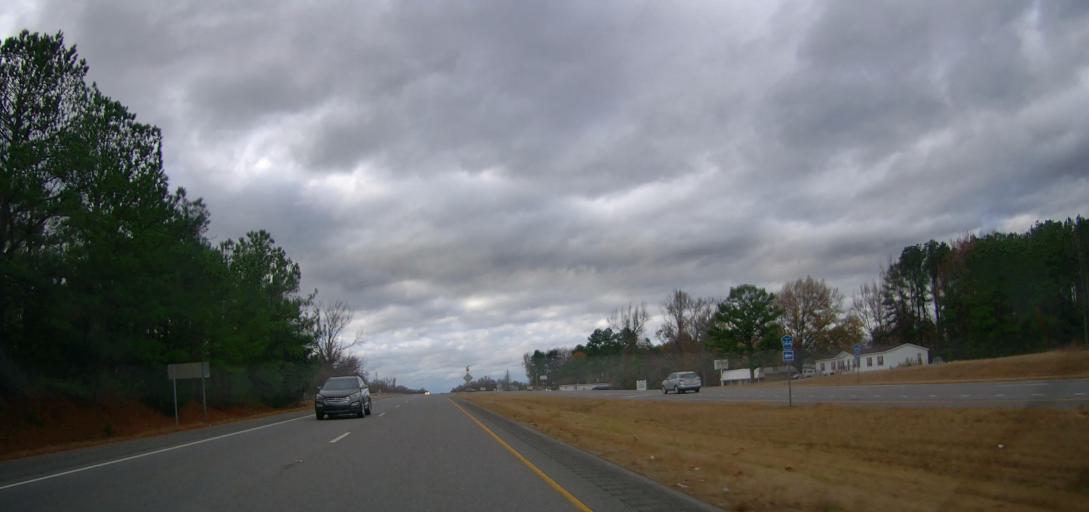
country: US
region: Alabama
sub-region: Lawrence County
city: Town Creek
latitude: 34.5905
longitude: -87.4270
